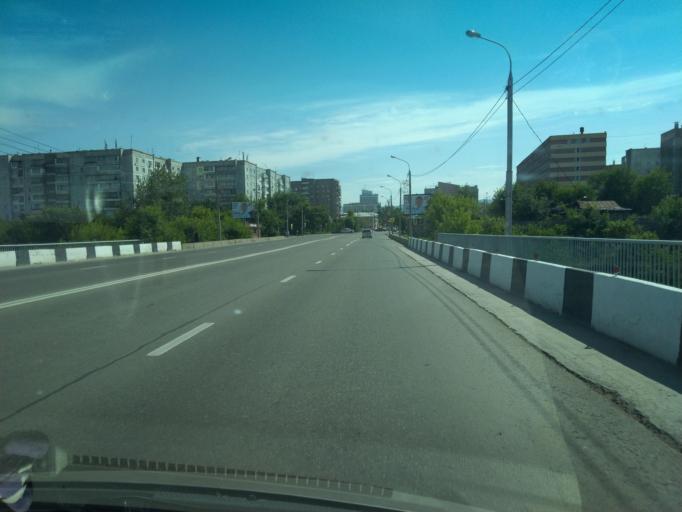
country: RU
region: Krasnoyarskiy
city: Krasnoyarsk
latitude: 56.0173
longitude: 92.8699
